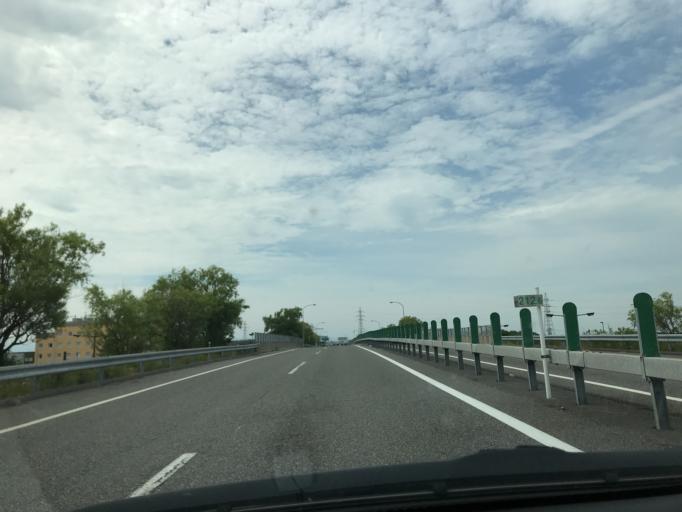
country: JP
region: Niigata
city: Niigata-shi
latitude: 37.8774
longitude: 139.0375
